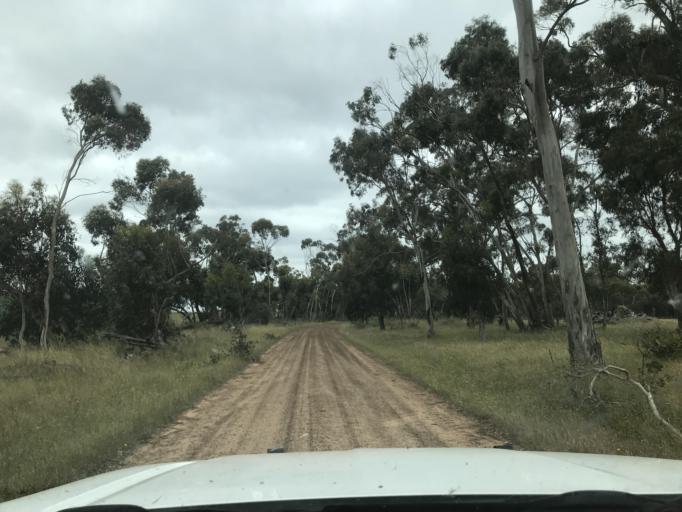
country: AU
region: South Australia
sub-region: Wattle Range
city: Penola
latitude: -37.2447
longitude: 141.1265
